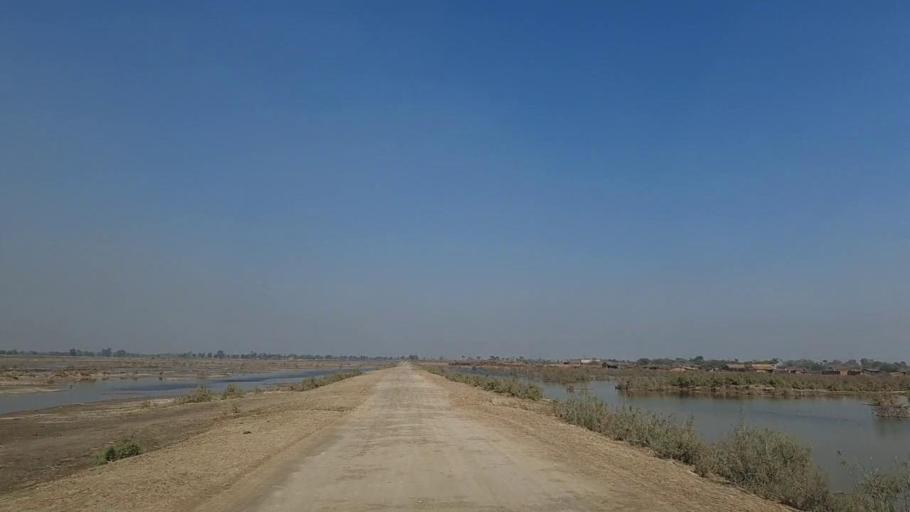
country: PK
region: Sindh
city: Daur
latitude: 26.4736
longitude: 68.3253
